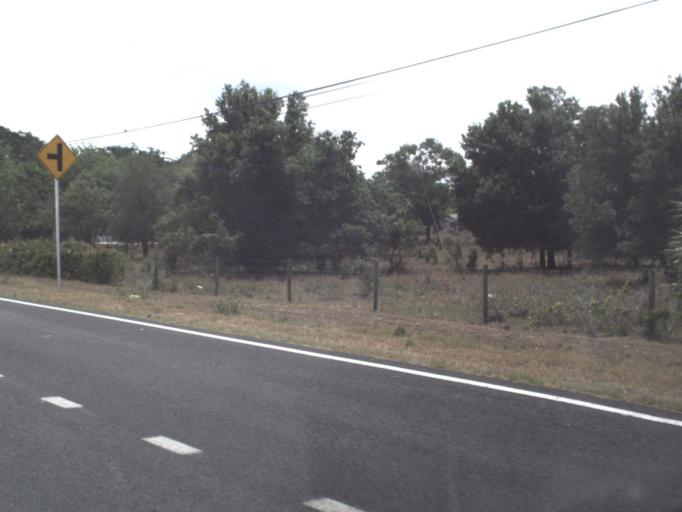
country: US
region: Florida
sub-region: Lake County
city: Groveland
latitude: 28.5579
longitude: -81.8240
